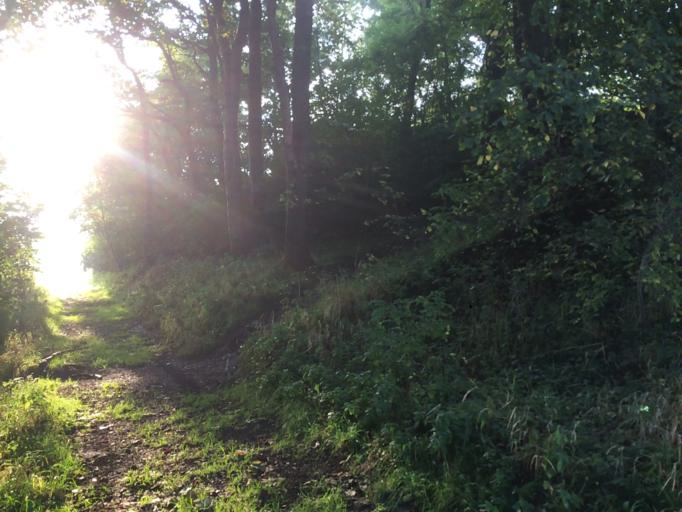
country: GB
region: Scotland
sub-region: Edinburgh
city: Colinton
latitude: 55.9175
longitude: -3.2318
